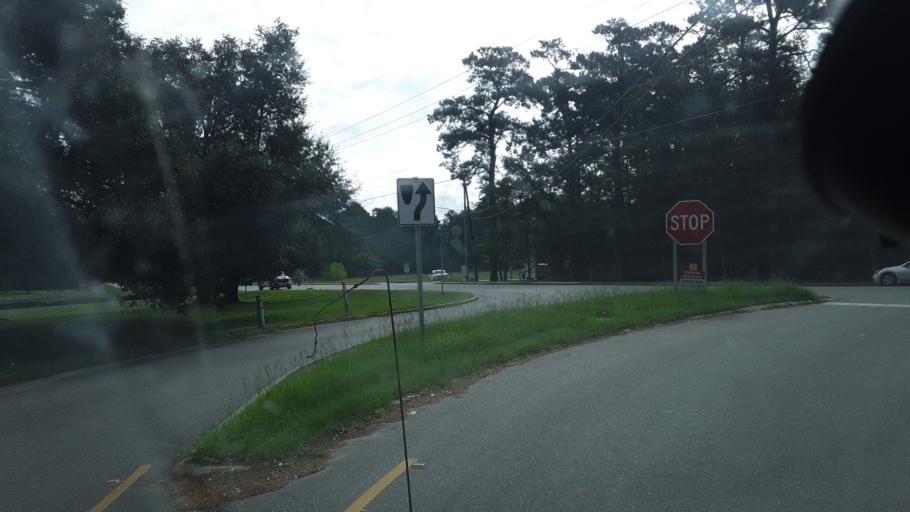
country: US
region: South Carolina
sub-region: Horry County
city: Conway
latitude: 33.8231
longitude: -79.0758
